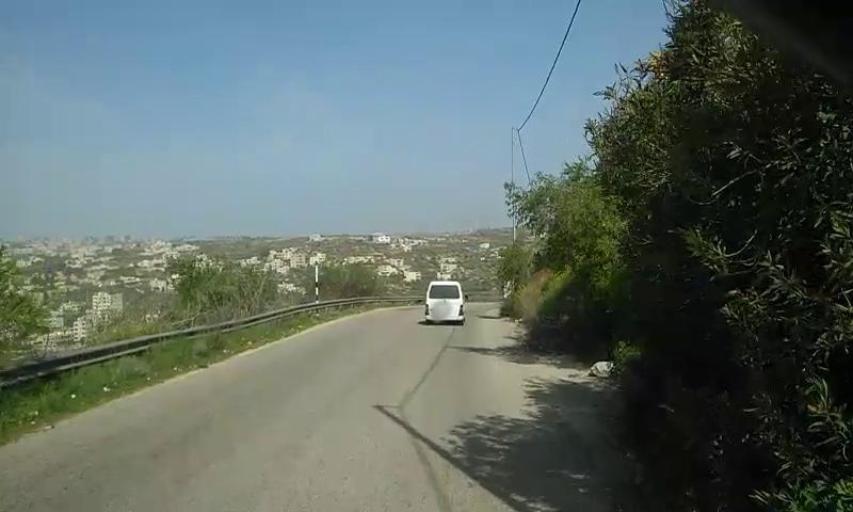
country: PS
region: West Bank
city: Dura al Qar`
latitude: 31.9593
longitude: 35.2249
